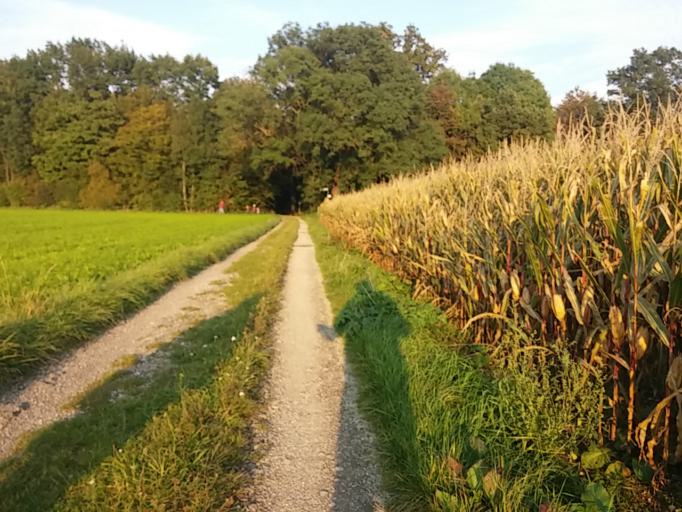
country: DE
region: Bavaria
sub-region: Upper Bavaria
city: Zorneding
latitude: 48.0981
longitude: 11.8381
